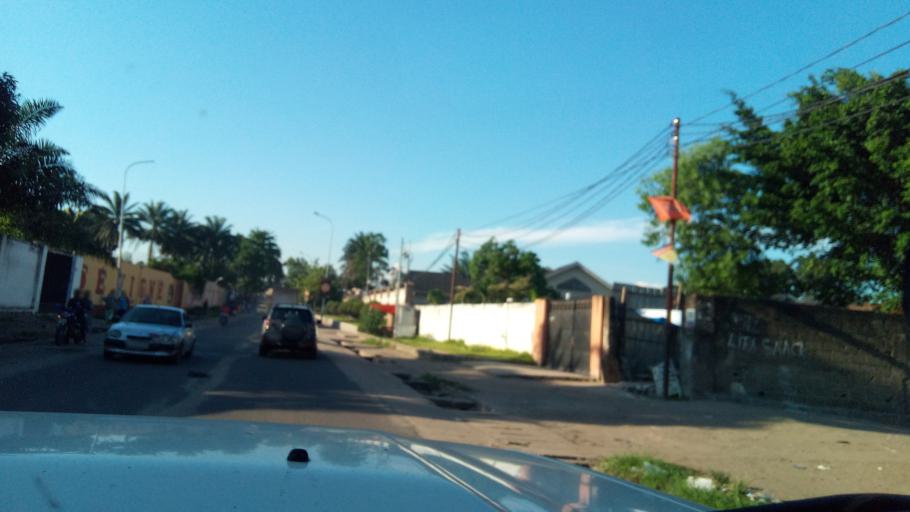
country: CD
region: Kinshasa
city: Kinshasa
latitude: -4.3492
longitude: 15.2646
